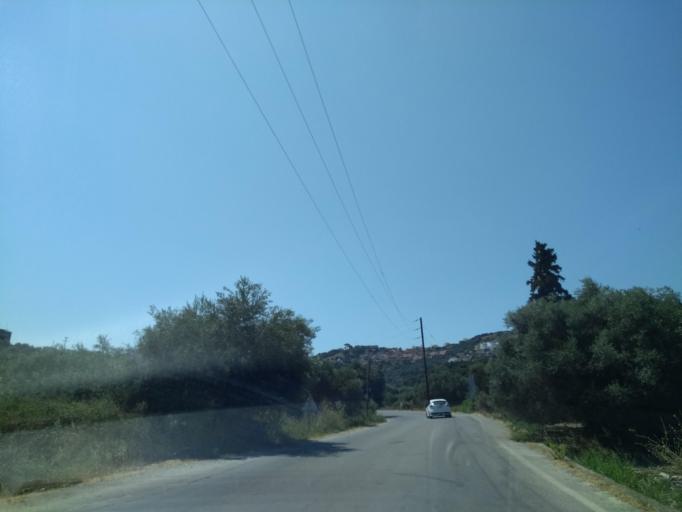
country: GR
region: Crete
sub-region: Nomos Chanias
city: Georgioupolis
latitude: 35.3686
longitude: 24.2527
